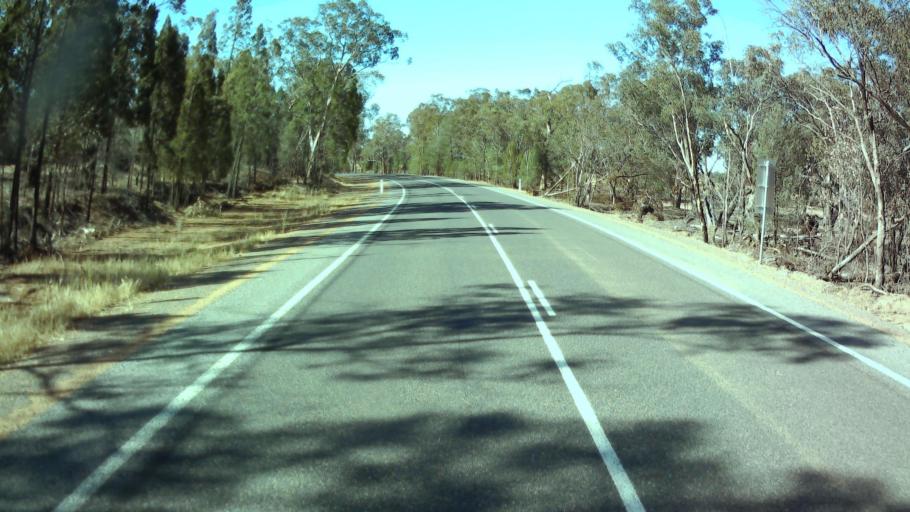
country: AU
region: New South Wales
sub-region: Weddin
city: Grenfell
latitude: -33.7460
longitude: 148.0878
